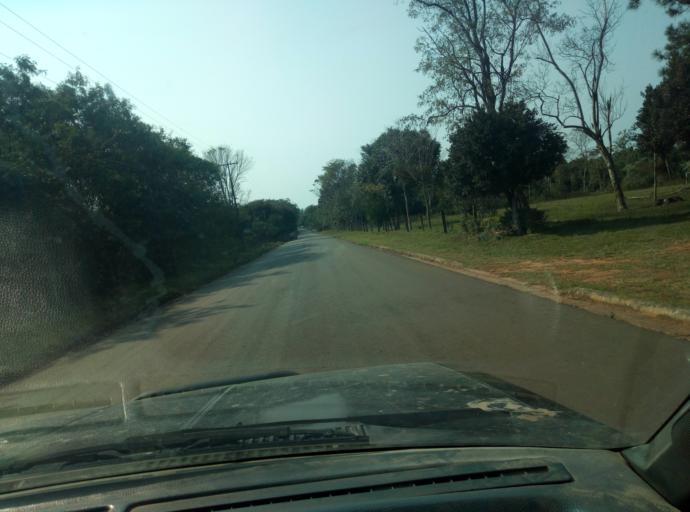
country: PY
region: Caaguazu
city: Carayao
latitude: -25.2102
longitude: -56.3038
